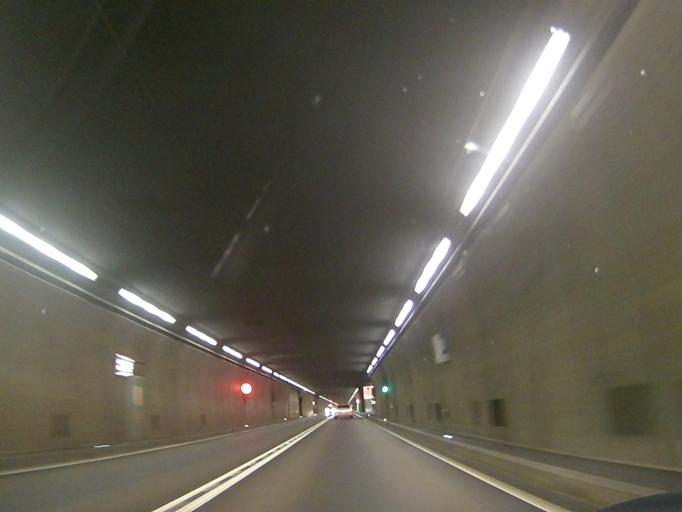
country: CH
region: Uri
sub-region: Uri
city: Andermatt
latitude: 46.6449
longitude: 8.5818
